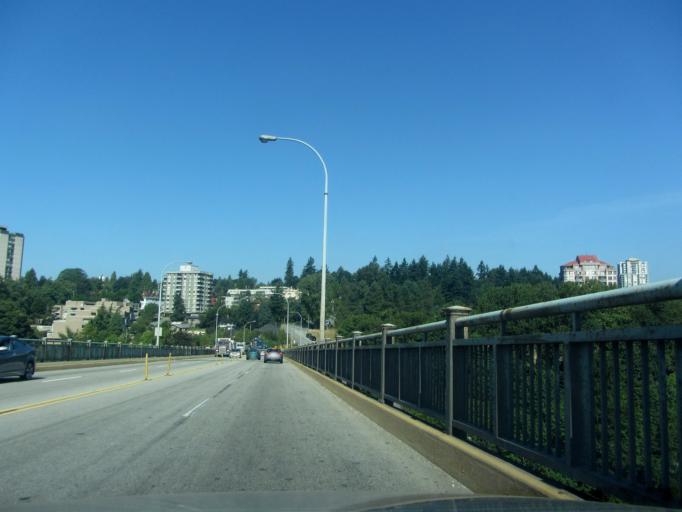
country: CA
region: British Columbia
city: New Westminster
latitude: 49.2086
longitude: -122.8969
